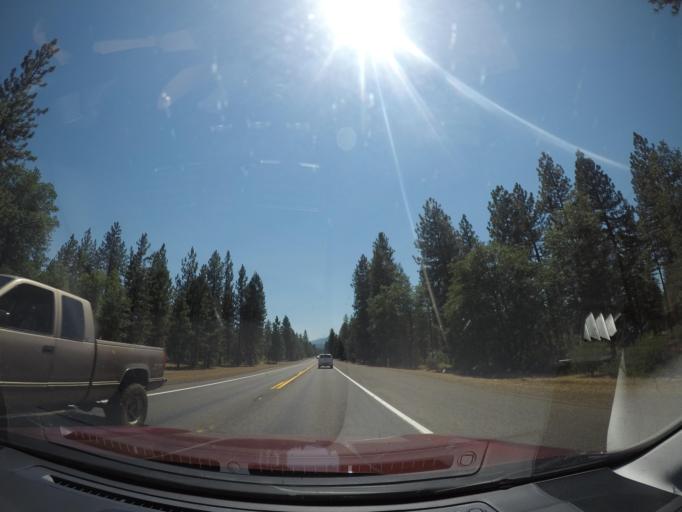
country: US
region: California
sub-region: Shasta County
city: Burney
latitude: 40.9005
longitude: -121.6432
